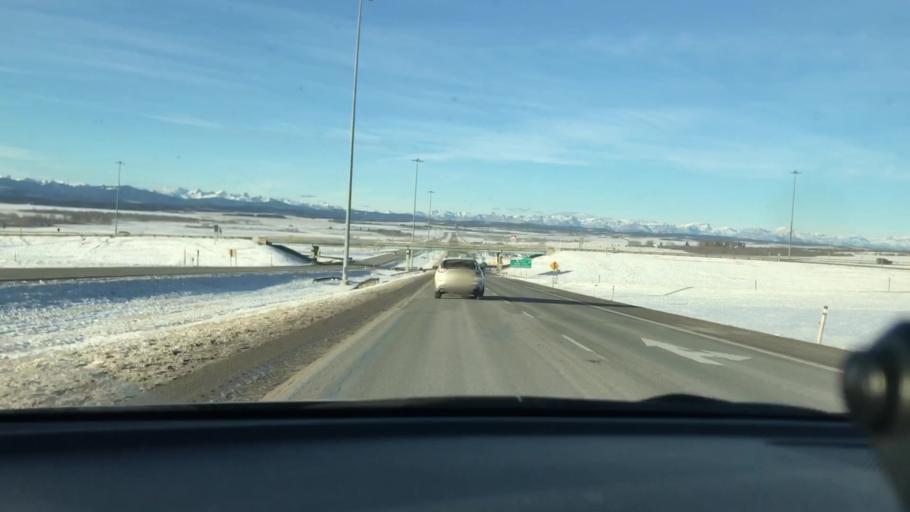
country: CA
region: Alberta
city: Cochrane
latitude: 51.0878
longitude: -114.4628
